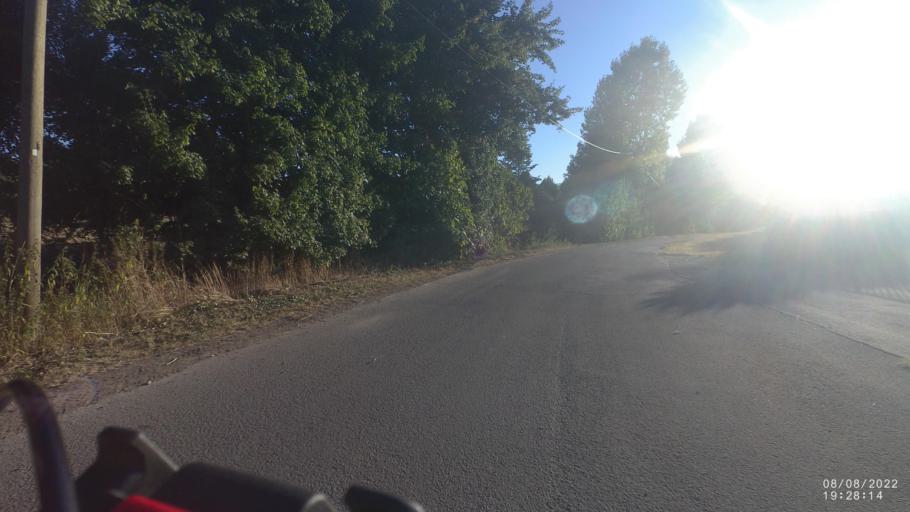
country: DE
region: Rheinland-Pfalz
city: Ober-Saulheim
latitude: 49.8627
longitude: 8.1282
